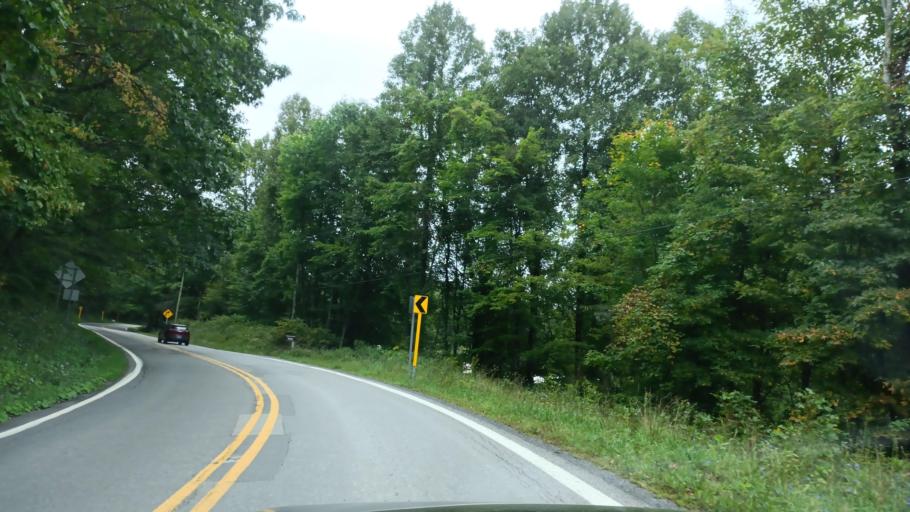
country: US
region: West Virginia
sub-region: Preston County
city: Kingwood
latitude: 39.3328
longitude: -79.7370
